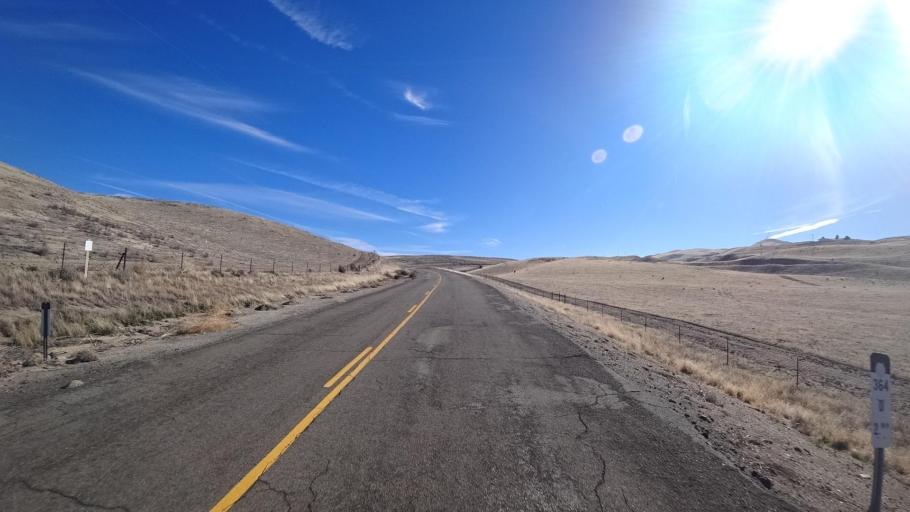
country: US
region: California
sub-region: Kern County
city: Maricopa
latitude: 34.9469
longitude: -119.4156
